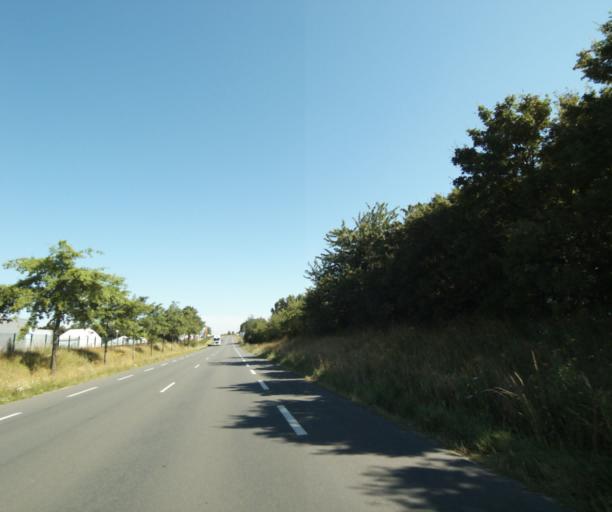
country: FR
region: Pays de la Loire
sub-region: Departement de la Mayenne
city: Laval
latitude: 48.0578
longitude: -0.7332
